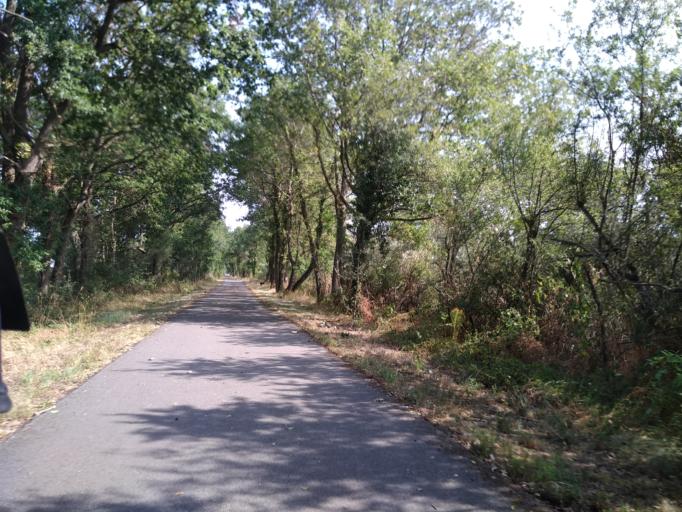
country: FR
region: Bourgogne
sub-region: Departement de Saone-et-Loire
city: Marcigny
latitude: 46.3166
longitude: 4.0284
